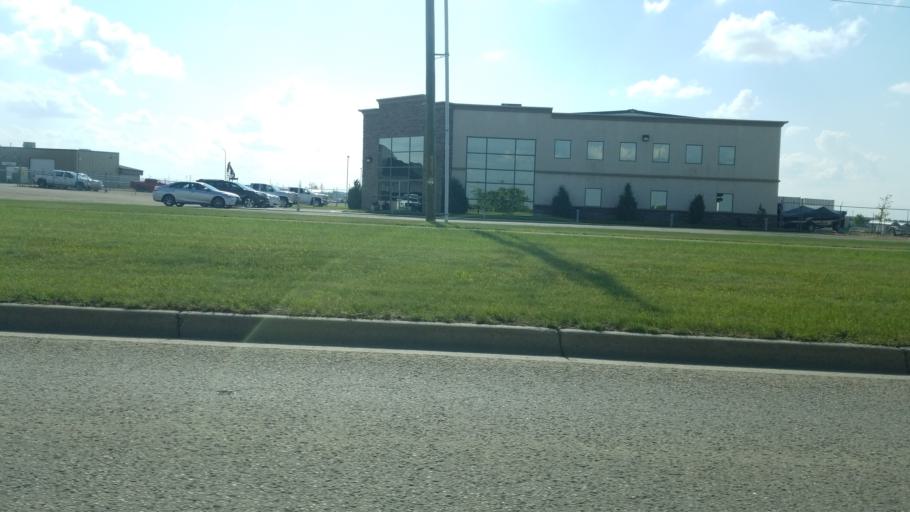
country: CA
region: Saskatchewan
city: Lloydminster
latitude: 53.2957
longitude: -110.0340
